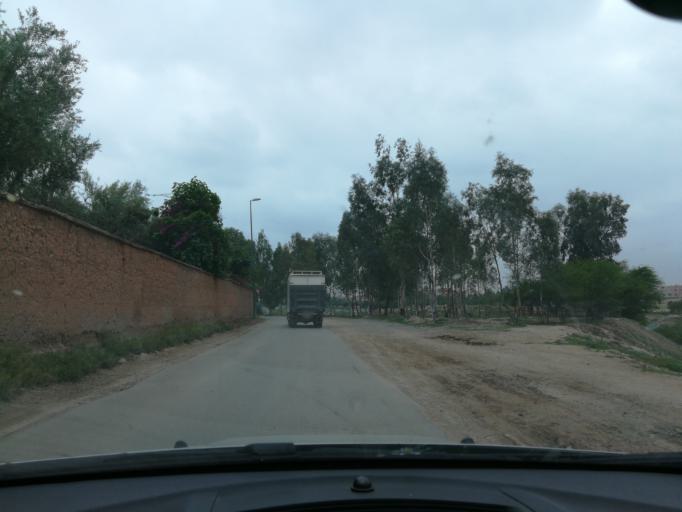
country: MA
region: Marrakech-Tensift-Al Haouz
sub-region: Marrakech
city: Marrakesh
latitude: 31.6597
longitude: -7.9832
